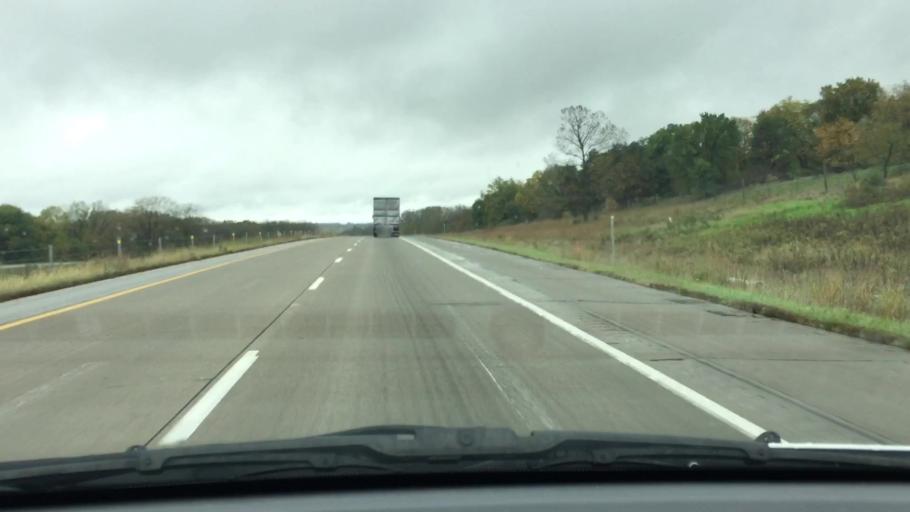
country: US
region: Iowa
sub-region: Jasper County
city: Colfax
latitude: 41.6866
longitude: -93.2764
